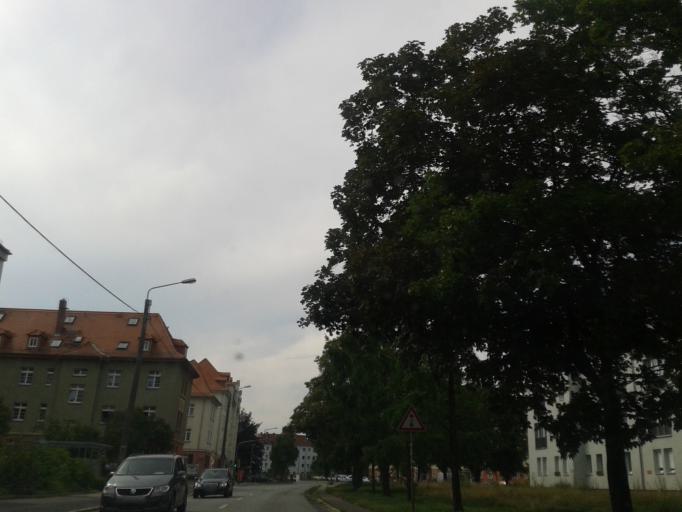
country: DE
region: Saxony
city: Dresden
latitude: 51.0818
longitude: 13.7086
